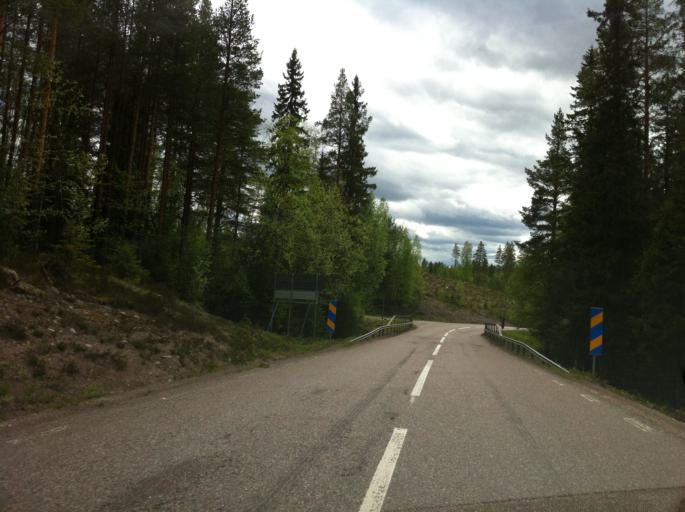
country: NO
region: Hedmark
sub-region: Trysil
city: Innbygda
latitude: 61.5124
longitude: 13.0840
